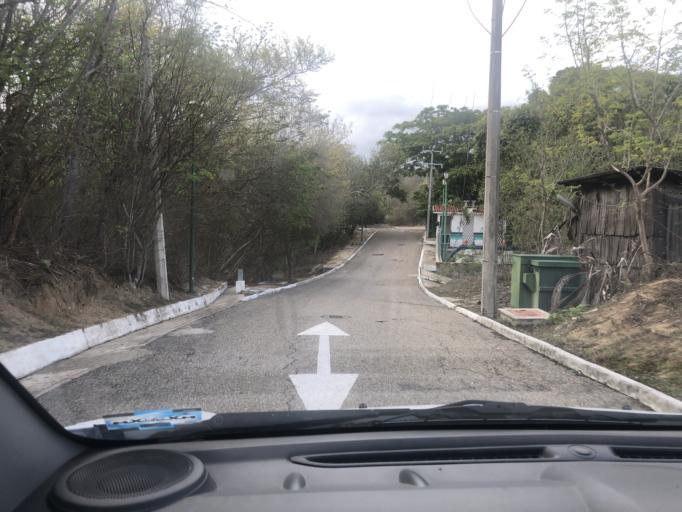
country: MX
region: Oaxaca
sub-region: Santa Maria Huatulco
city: Crucecita
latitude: 15.7731
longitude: -96.0868
